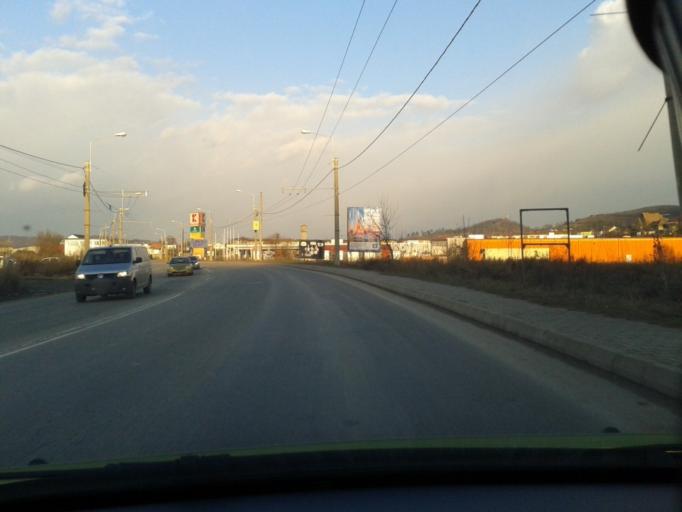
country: RO
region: Sibiu
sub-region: Comuna Tarnava
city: Tarnava
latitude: 46.1430
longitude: 24.3202
